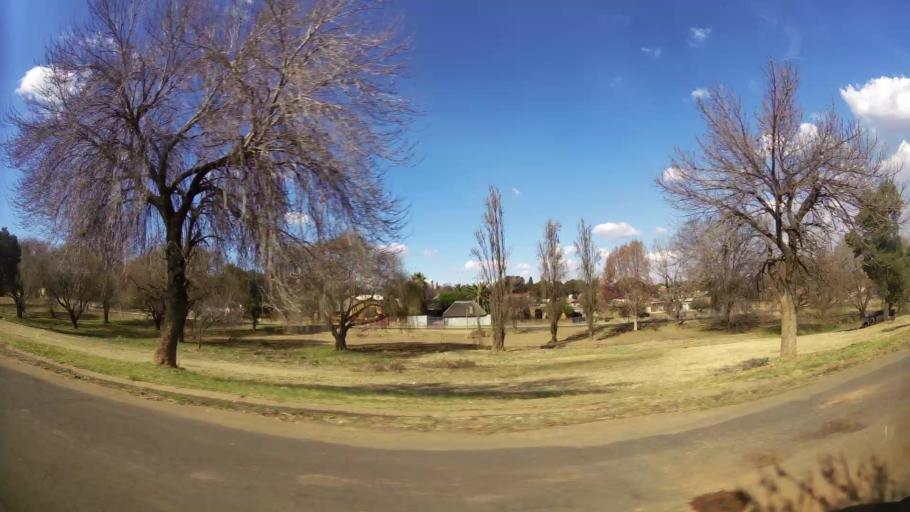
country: ZA
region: Mpumalanga
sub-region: Nkangala District Municipality
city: Witbank
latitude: -25.9089
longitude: 29.2346
